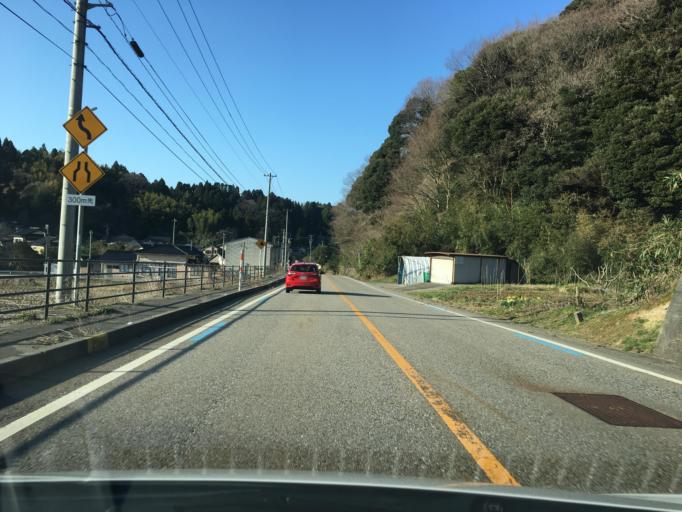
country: JP
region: Toyama
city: Himi
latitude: 36.9298
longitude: 137.0262
